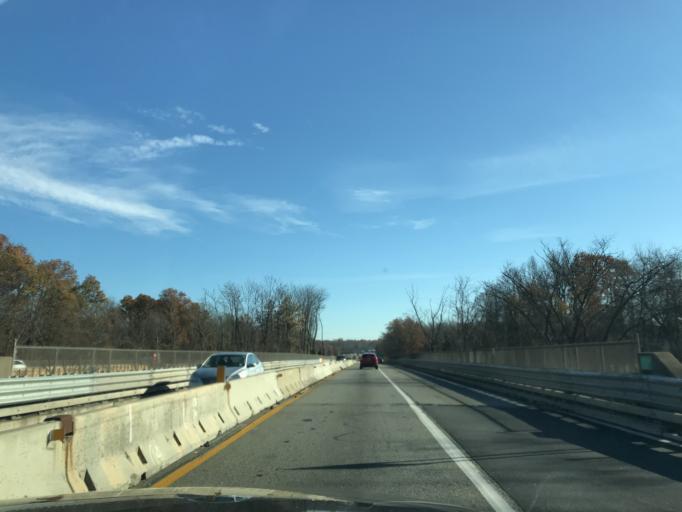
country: US
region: New Jersey
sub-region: Essex County
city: West Caldwell
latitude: 40.8310
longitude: -74.3308
